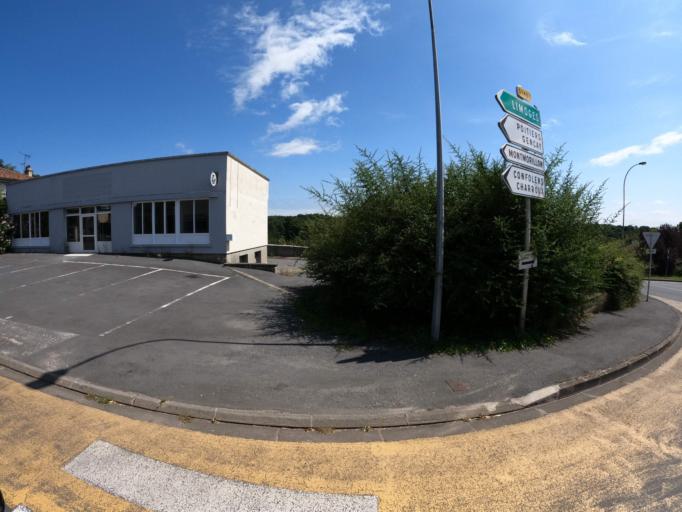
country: FR
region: Poitou-Charentes
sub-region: Departement de la Vienne
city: Civray
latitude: 46.1511
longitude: 0.2959
